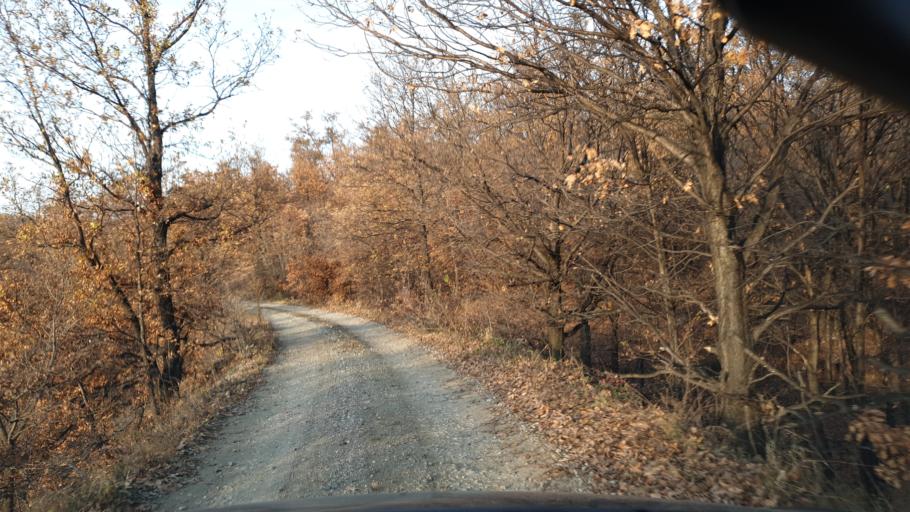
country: RS
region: Central Serbia
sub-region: Borski Okrug
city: Bor
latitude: 44.0705
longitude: 22.0757
